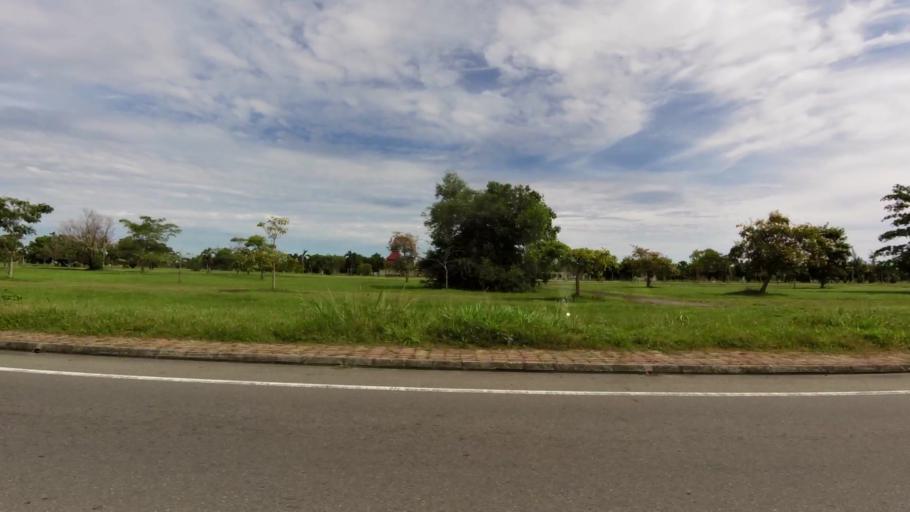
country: BN
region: Belait
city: Seria
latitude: 4.6149
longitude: 114.3276
